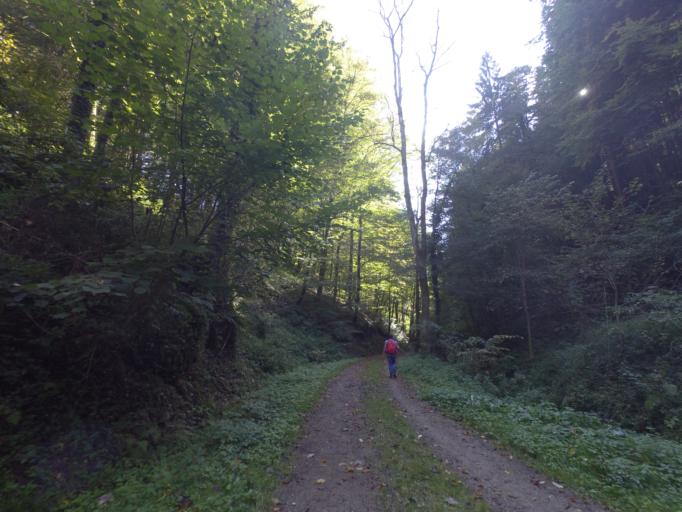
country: AT
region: Styria
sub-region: Politischer Bezirk Leibnitz
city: Kitzeck im Sausal
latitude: 46.7873
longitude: 15.4381
